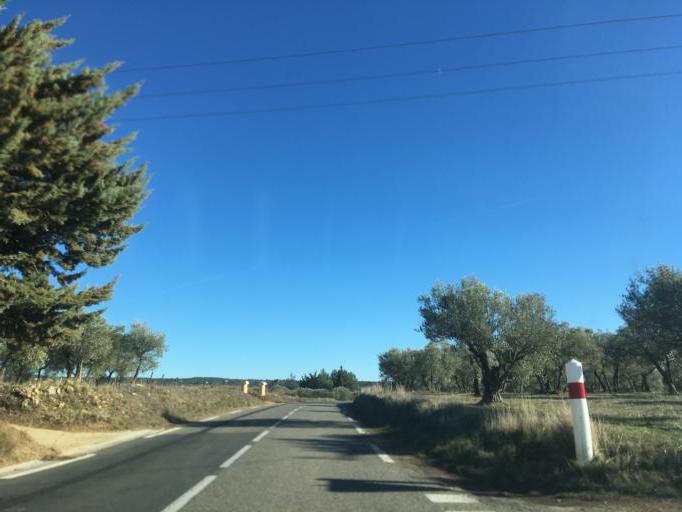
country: FR
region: Provence-Alpes-Cote d'Azur
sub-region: Departement du Var
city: Barjols
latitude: 43.5958
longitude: 5.9951
